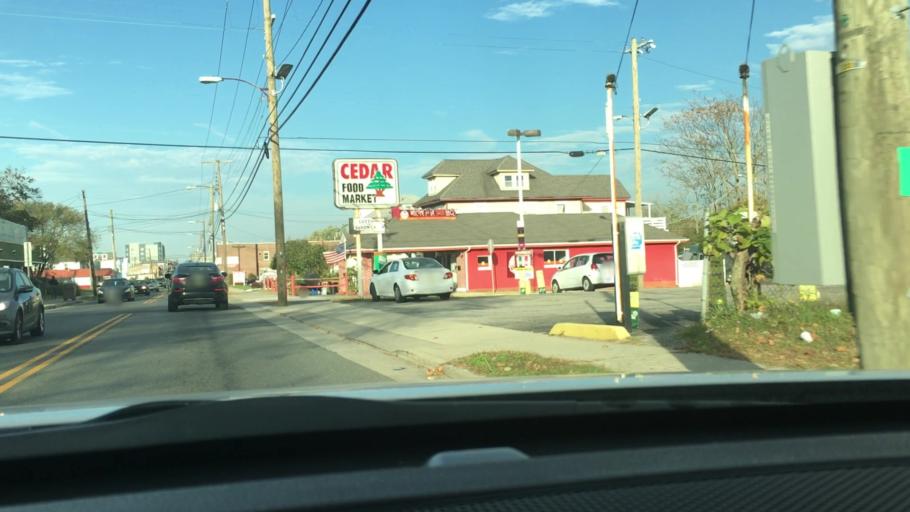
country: US
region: New Jersey
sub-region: Atlantic County
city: Pleasantville
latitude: 39.3865
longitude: -74.5272
